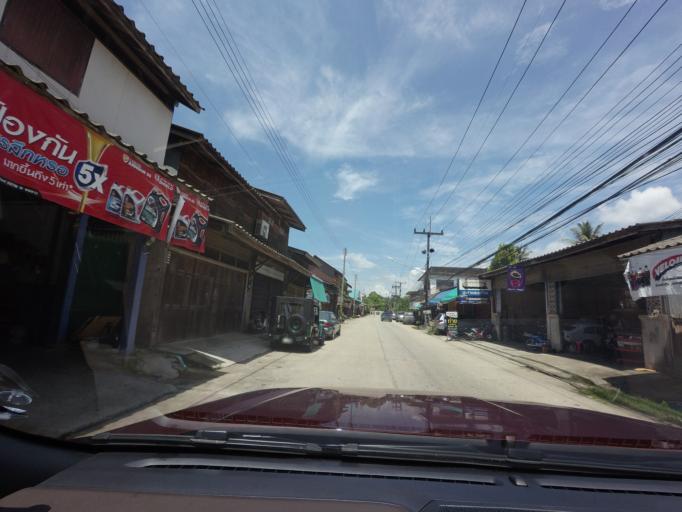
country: TH
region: Narathiwat
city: Ra-ngae
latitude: 6.2899
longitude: 101.7062
